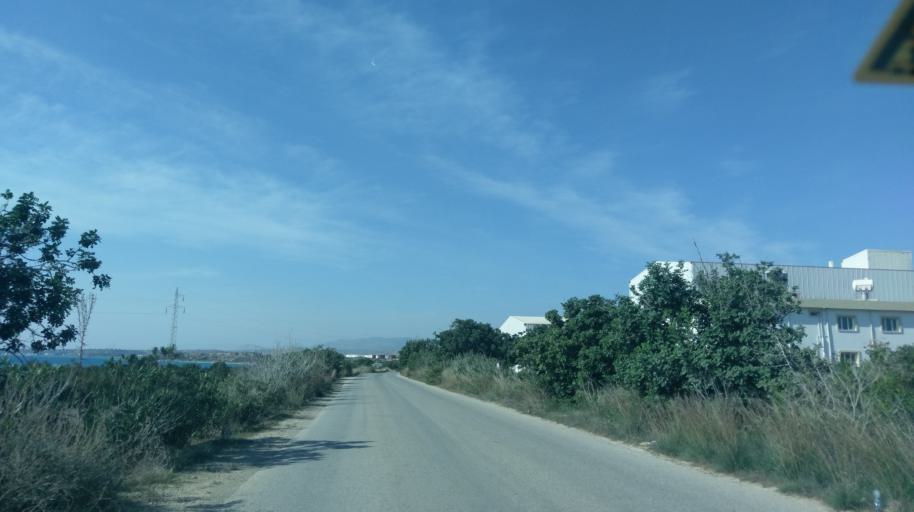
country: CY
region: Ammochostos
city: Trikomo
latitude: 35.3265
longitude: 34.0051
